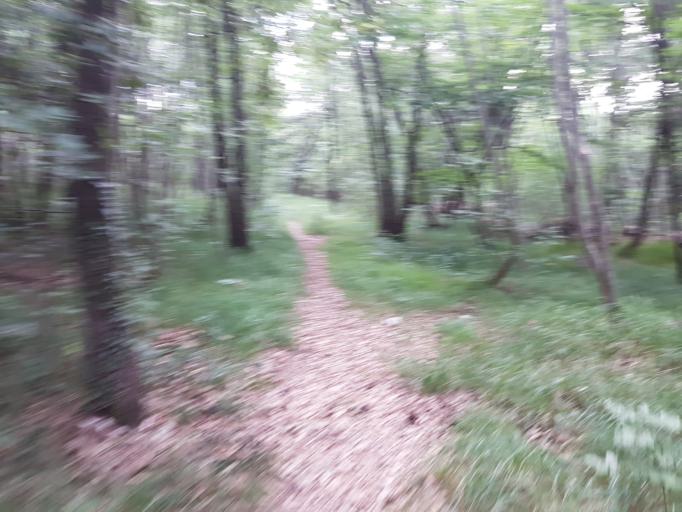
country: IT
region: Friuli Venezia Giulia
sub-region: Provincia di Trieste
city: Aurisina
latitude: 45.7460
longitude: 13.6712
